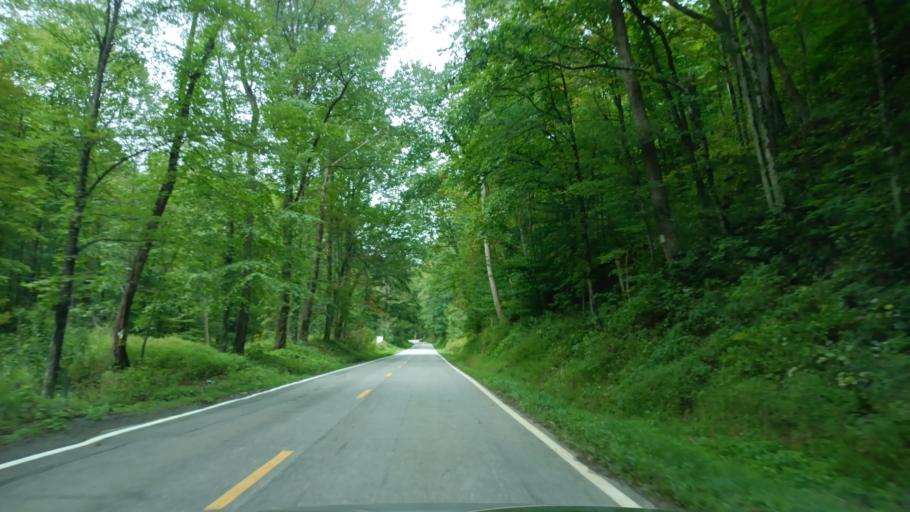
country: US
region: West Virginia
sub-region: Preston County
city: Kingwood
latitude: 39.3190
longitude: -79.7041
